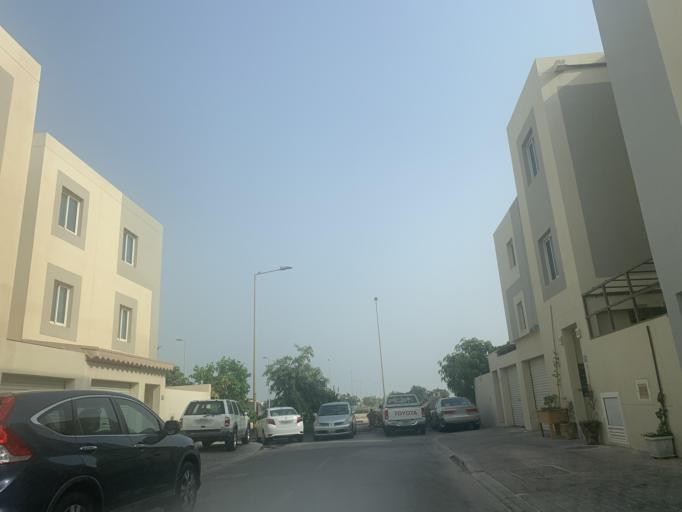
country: BH
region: Manama
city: Jidd Hafs
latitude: 26.2283
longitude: 50.4534
